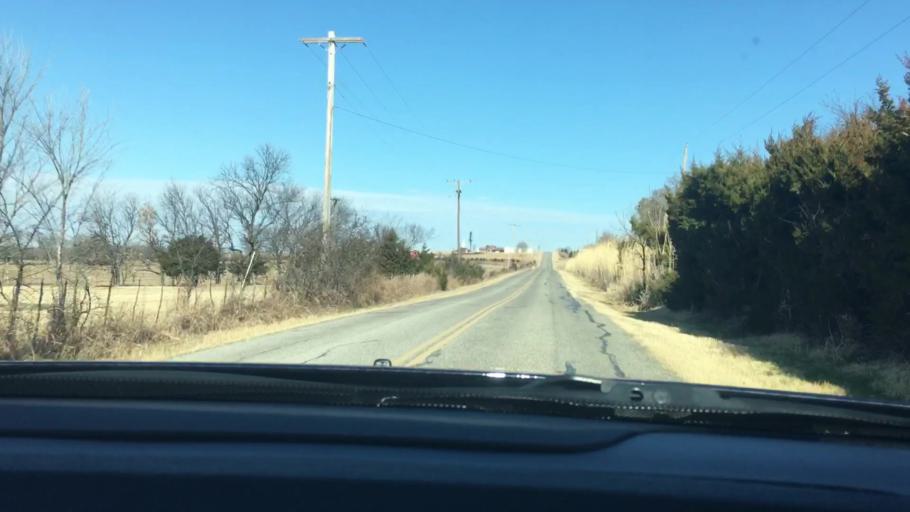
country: US
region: Oklahoma
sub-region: Murray County
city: Davis
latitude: 34.4981
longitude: -97.0553
